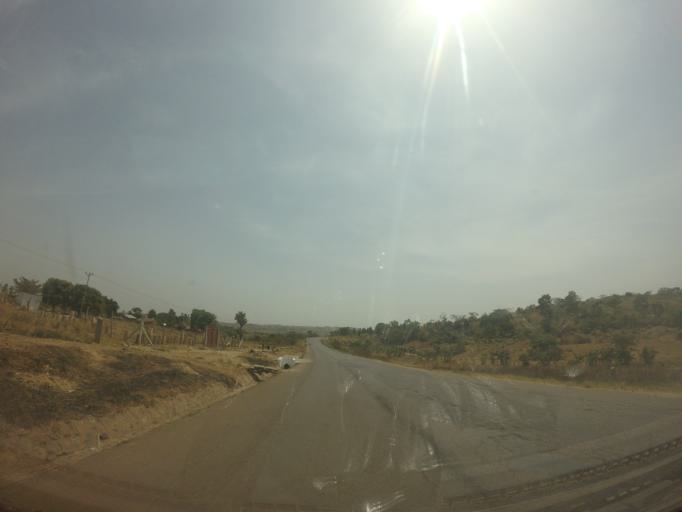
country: UG
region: Northern Region
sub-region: Arua District
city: Arua
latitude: 2.9494
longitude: 30.9353
